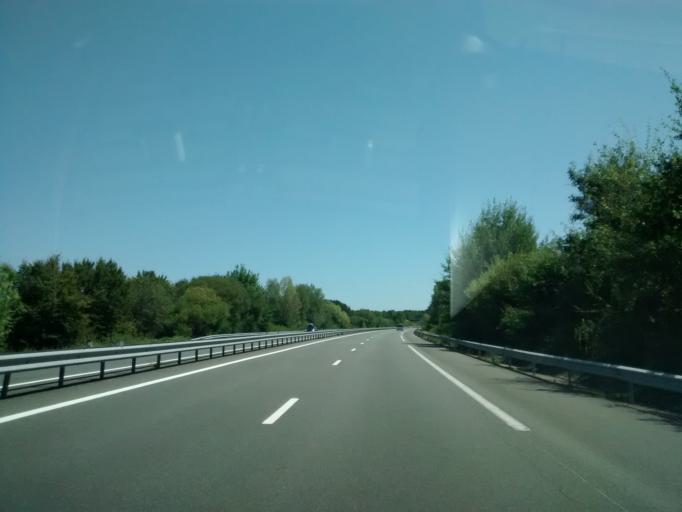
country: FR
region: Aquitaine
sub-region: Departement de la Gironde
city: Saint-Medard-de-Guizieres
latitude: 45.0083
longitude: -0.0417
